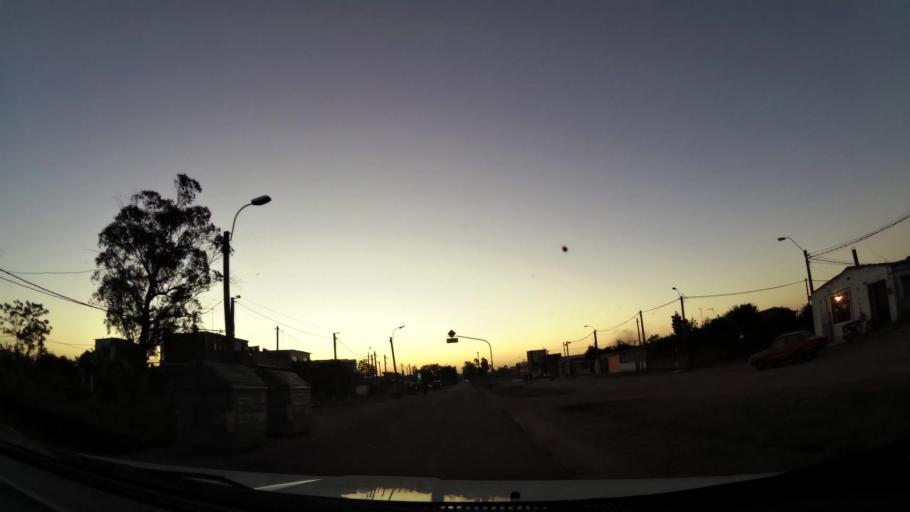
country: UY
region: Montevideo
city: Montevideo
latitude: -34.8223
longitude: -56.1596
